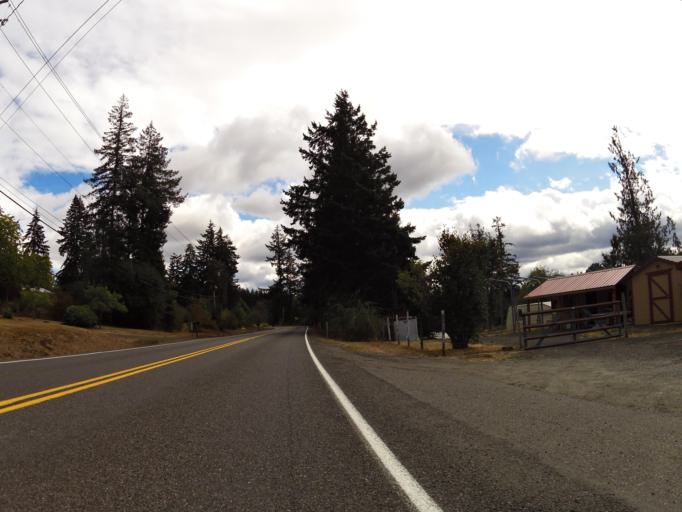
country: US
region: Washington
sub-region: Mason County
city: Shelton
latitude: 47.1803
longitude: -123.0909
